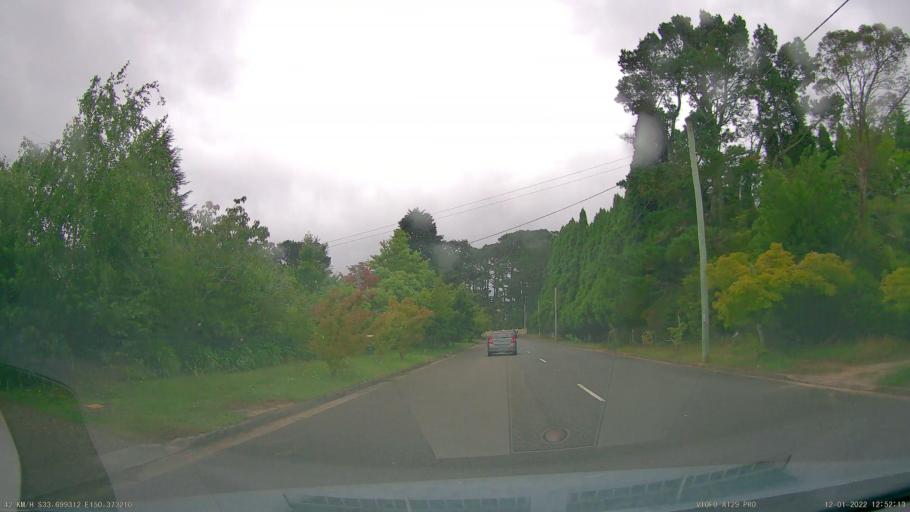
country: AU
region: New South Wales
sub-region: Blue Mountains Municipality
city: Leura
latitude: -33.6991
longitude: 150.3732
